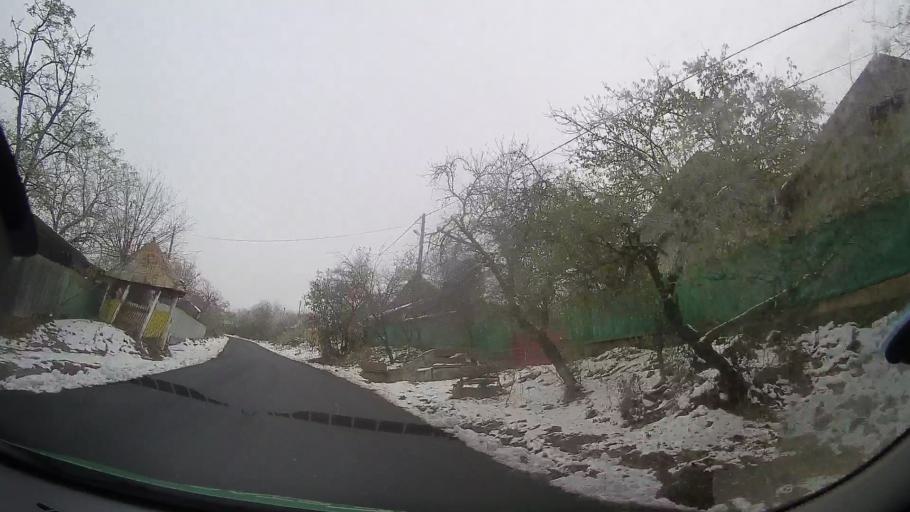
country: RO
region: Vaslui
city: Coroiesti
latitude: 46.2107
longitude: 27.4418
